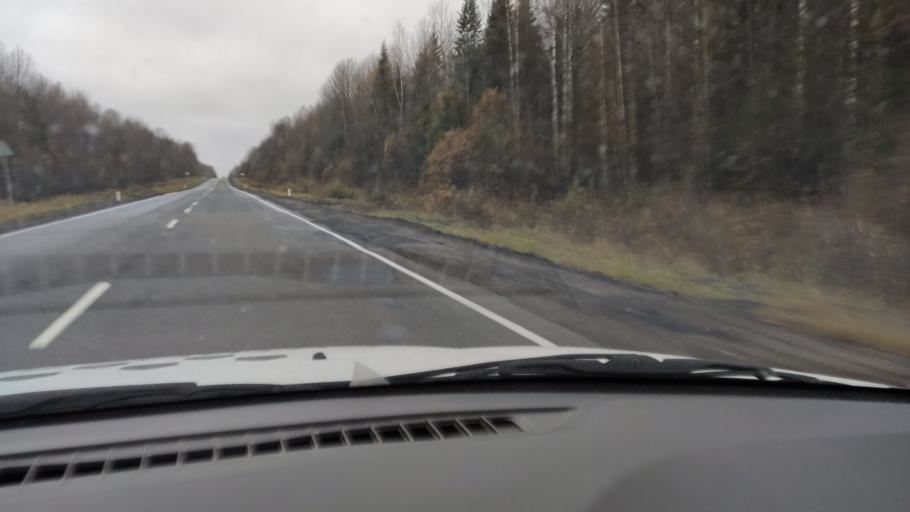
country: RU
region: Kirov
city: Omutninsk
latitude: 58.7568
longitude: 52.0313
